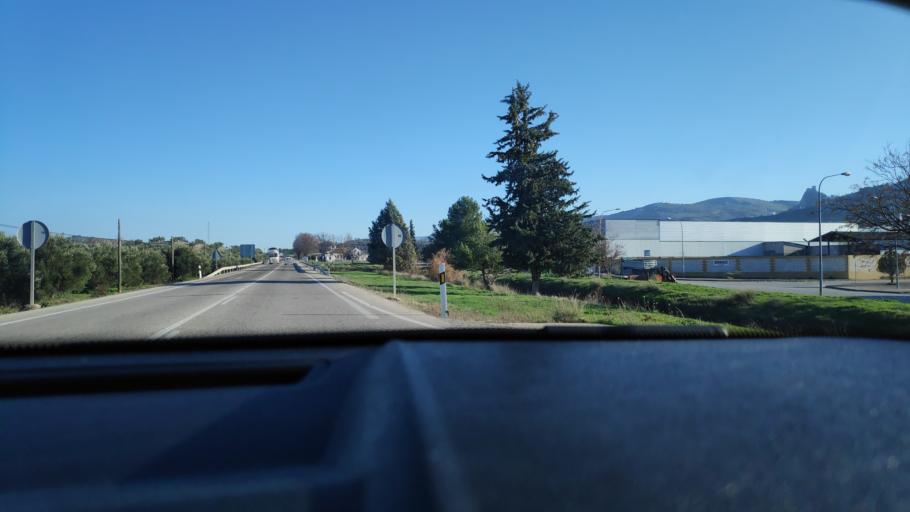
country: ES
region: Andalusia
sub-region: Province of Cordoba
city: Luque
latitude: 37.5813
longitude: -4.2839
